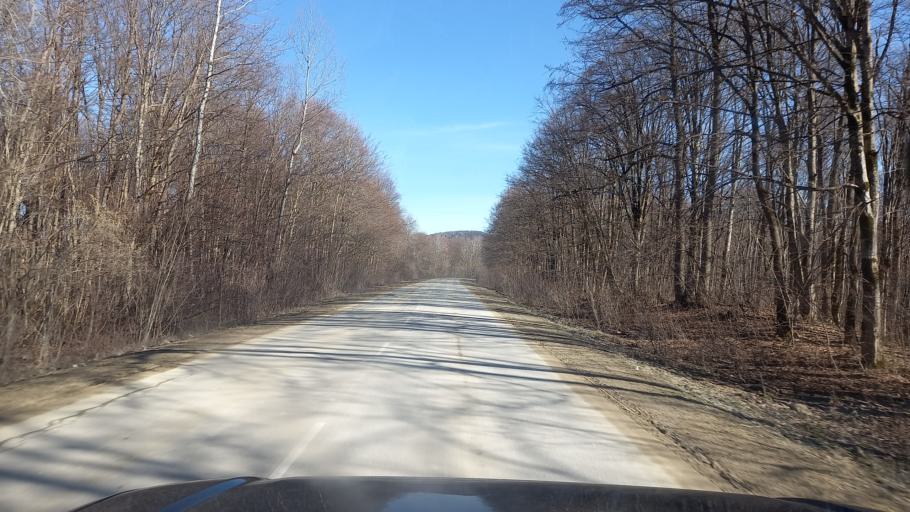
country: RU
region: Adygeya
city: Kamennomostskiy
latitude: 44.2820
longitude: 40.2505
